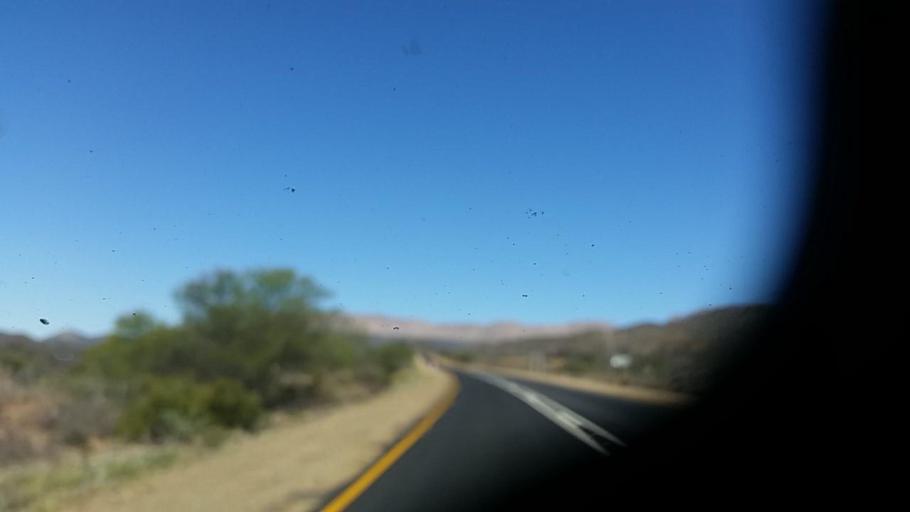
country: ZA
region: Western Cape
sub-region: Eden District Municipality
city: George
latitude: -33.5403
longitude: 22.7248
